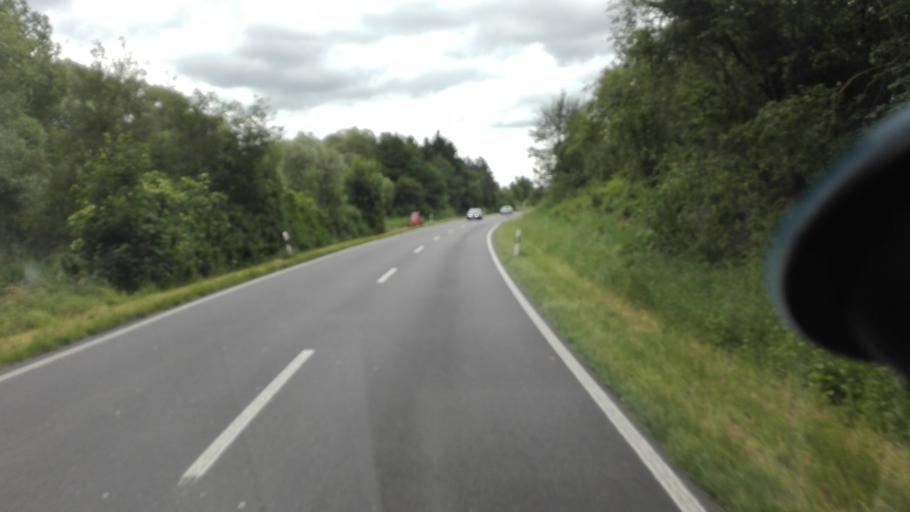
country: DE
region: Baden-Wuerttemberg
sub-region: Karlsruhe Region
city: Ubstadt-Weiher
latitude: 49.1812
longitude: 8.6307
